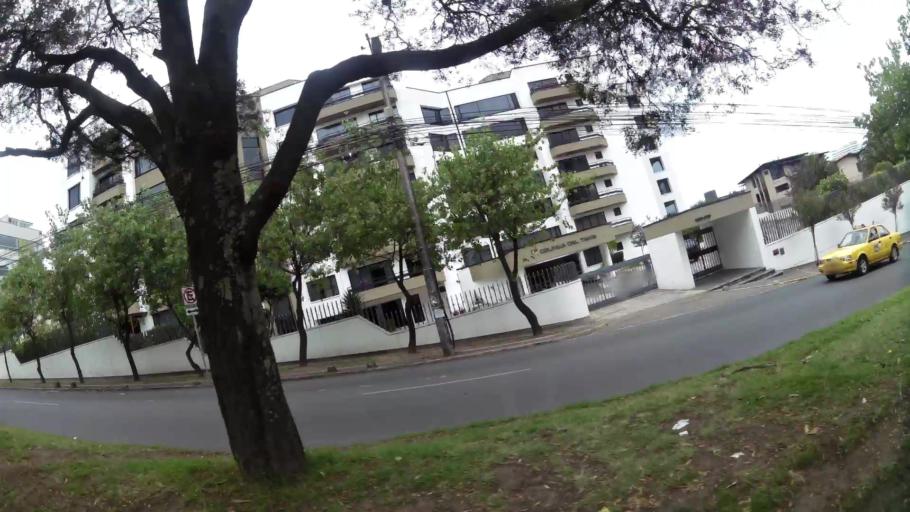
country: EC
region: Pichincha
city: Quito
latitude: -0.1685
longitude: -78.4900
